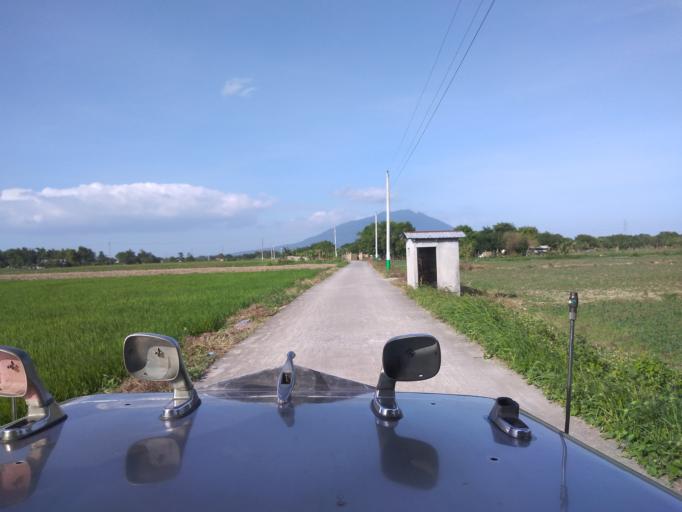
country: PH
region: Central Luzon
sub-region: Province of Pampanga
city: Bulaon
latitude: 15.0951
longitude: 120.6935
